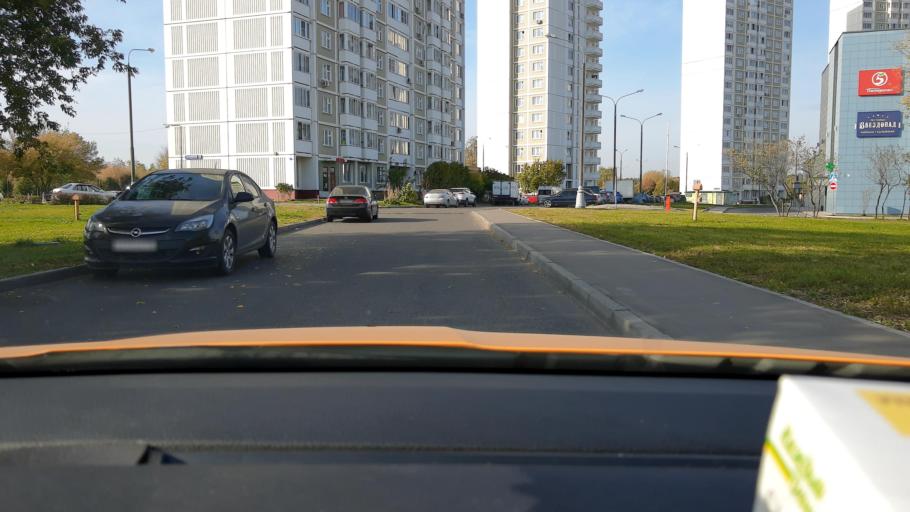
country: RU
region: Moscow
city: Kuz'minki
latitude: 55.6761
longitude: 37.8006
